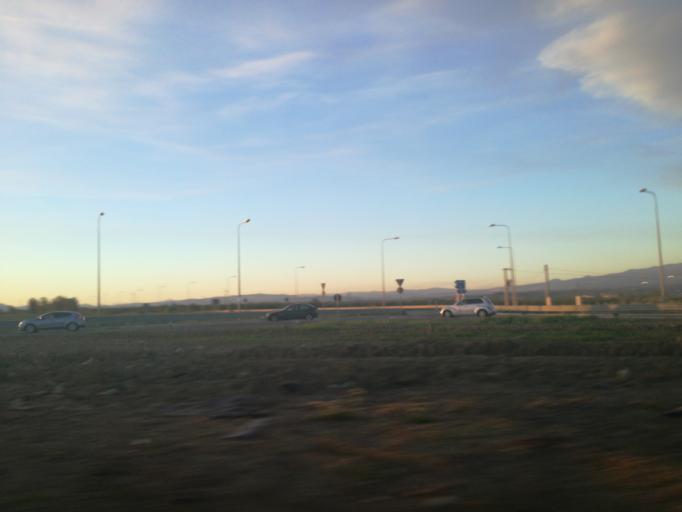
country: IT
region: Sicily
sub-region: Catania
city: Motta Sant'Anastasia
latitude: 37.4290
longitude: 14.9358
